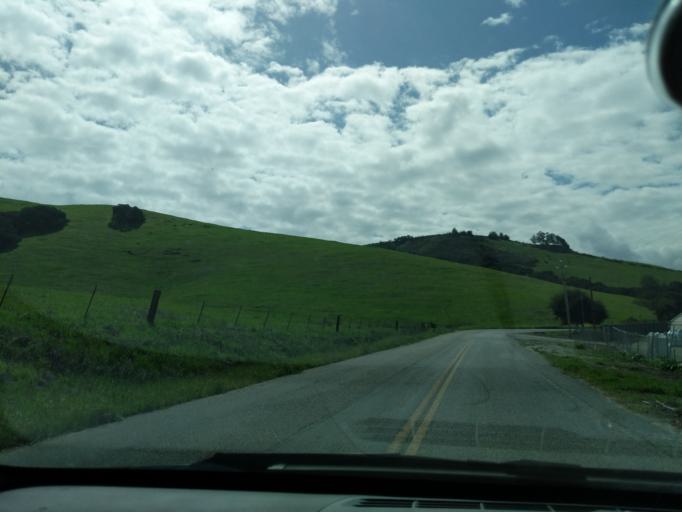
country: US
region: California
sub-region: Monterey County
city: Prunedale
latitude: 36.7628
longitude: -121.6018
